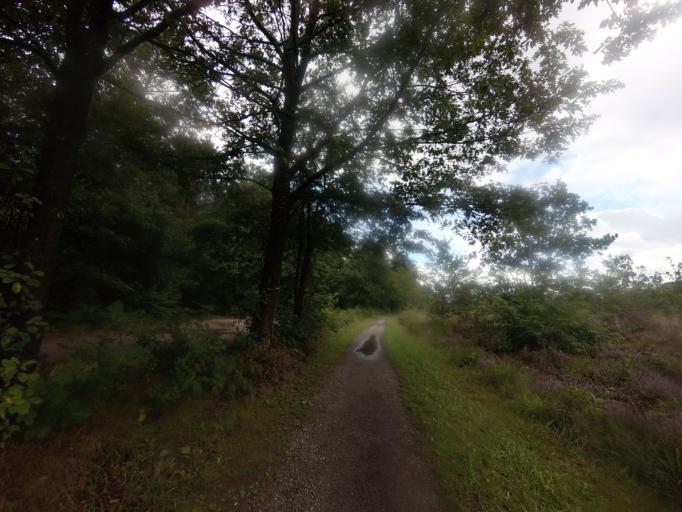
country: NL
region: Overijssel
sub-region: Gemeente Staphorst
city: Staphorst
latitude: 52.6393
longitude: 6.2699
